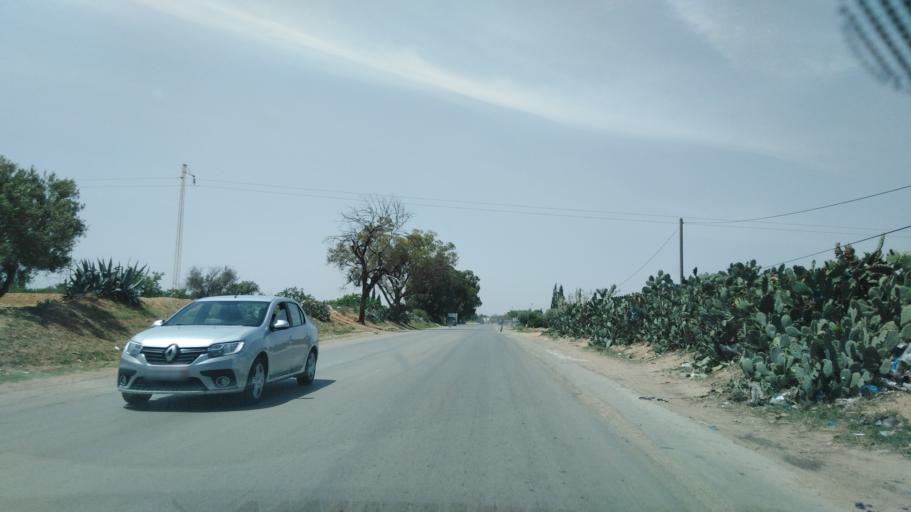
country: TN
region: Safaqis
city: Sfax
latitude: 34.7318
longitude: 10.5596
